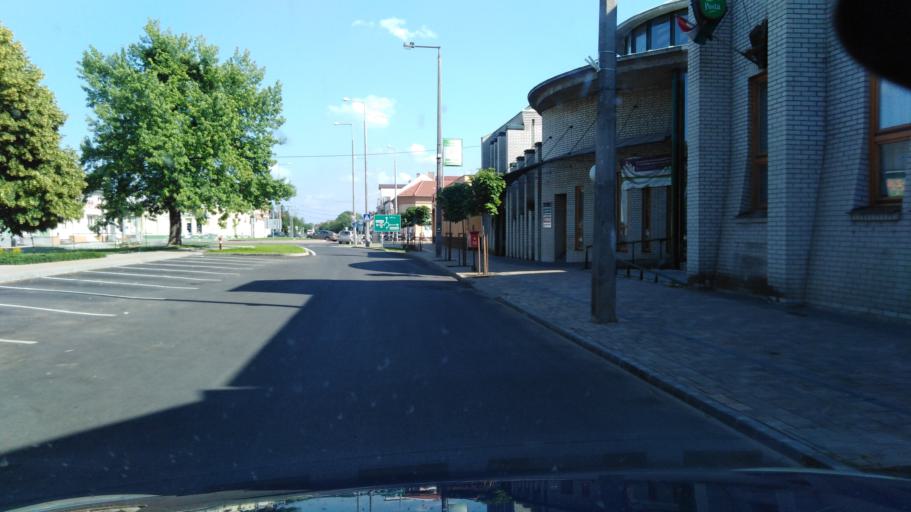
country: HU
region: Szabolcs-Szatmar-Bereg
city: Nyirbator
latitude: 47.8339
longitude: 22.1337
